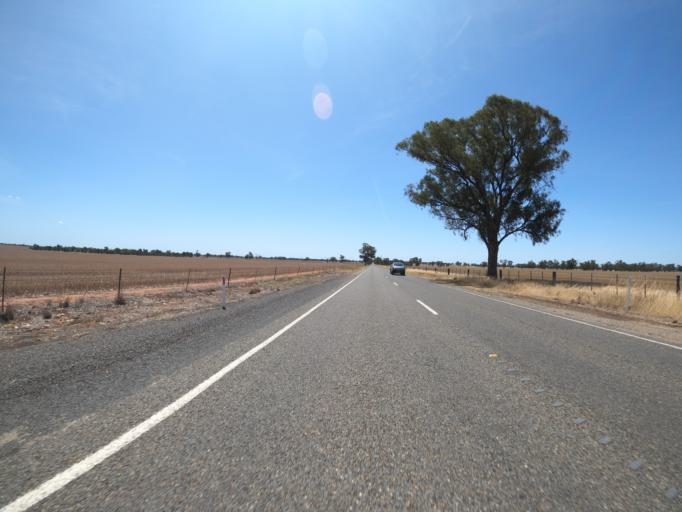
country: AU
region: Victoria
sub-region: Moira
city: Yarrawonga
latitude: -36.0767
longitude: 145.9954
